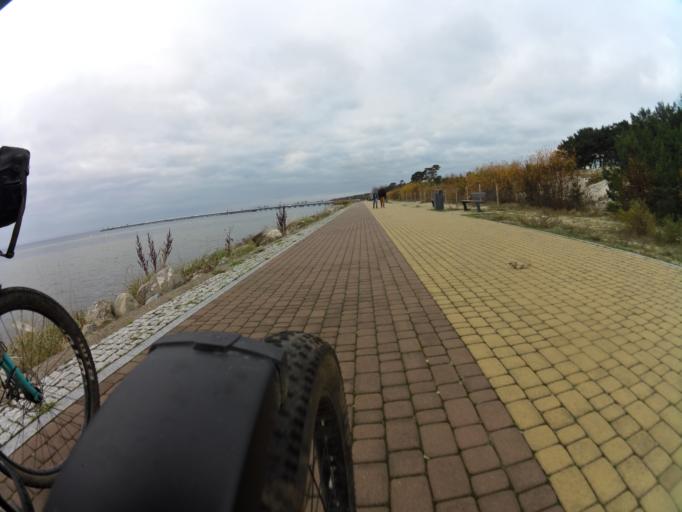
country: PL
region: Pomeranian Voivodeship
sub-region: Powiat pucki
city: Jastarnia
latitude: 54.6798
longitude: 18.7136
